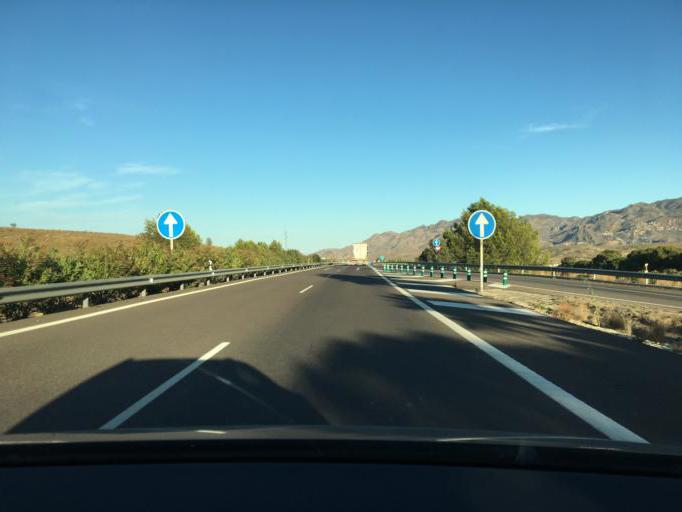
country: ES
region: Andalusia
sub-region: Provincia de Almeria
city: Bedar
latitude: 37.1474
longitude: -1.9819
